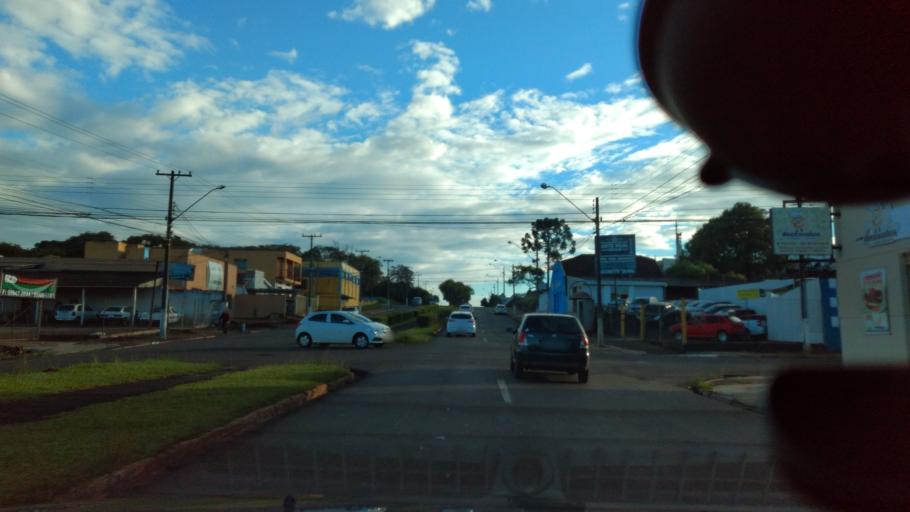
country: BR
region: Parana
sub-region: Guarapuava
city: Guarapuava
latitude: -25.3924
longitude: -51.4798
